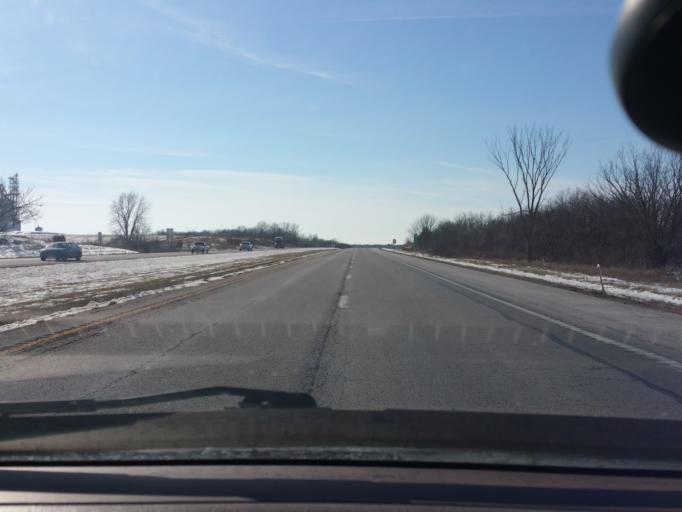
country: US
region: Missouri
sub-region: Harrison County
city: Bethany
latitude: 40.1133
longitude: -94.0641
